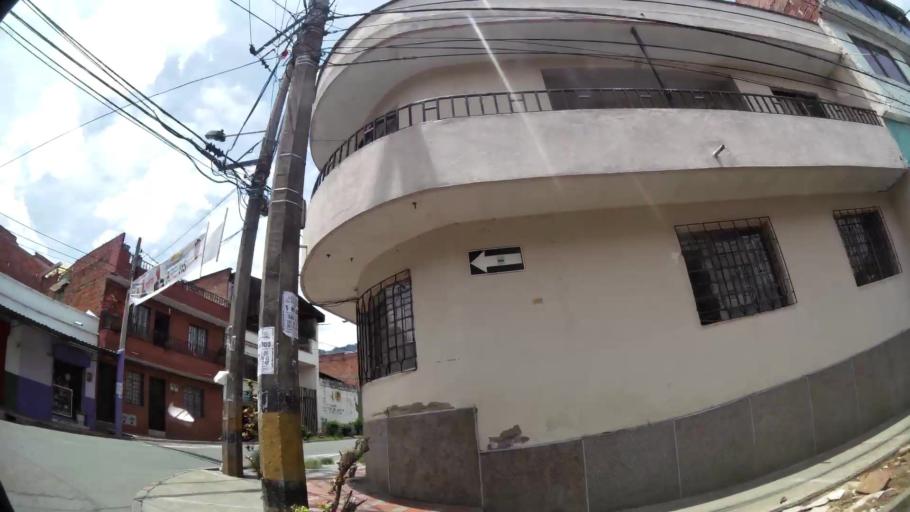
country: CO
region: Antioquia
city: Bello
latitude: 6.3386
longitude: -75.5624
